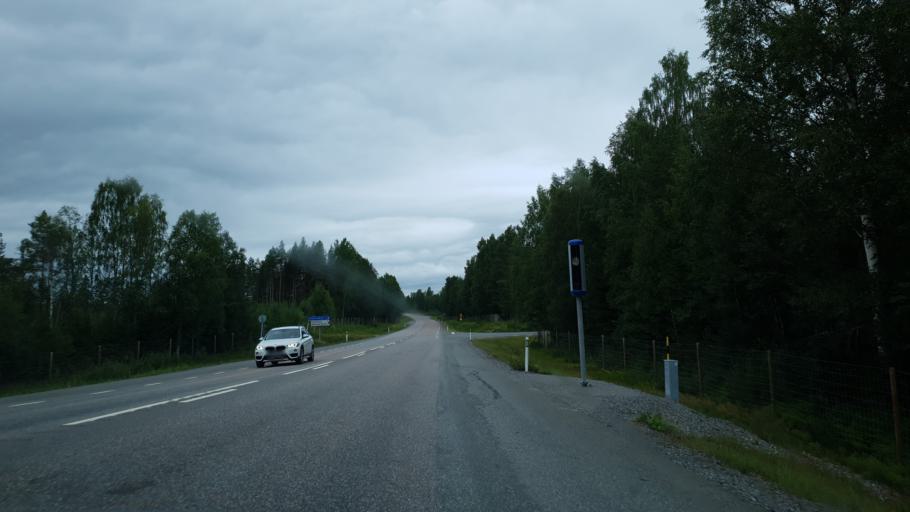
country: SE
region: Vaesterbotten
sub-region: Skelleftea Kommun
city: Viken
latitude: 64.7962
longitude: 20.7429
